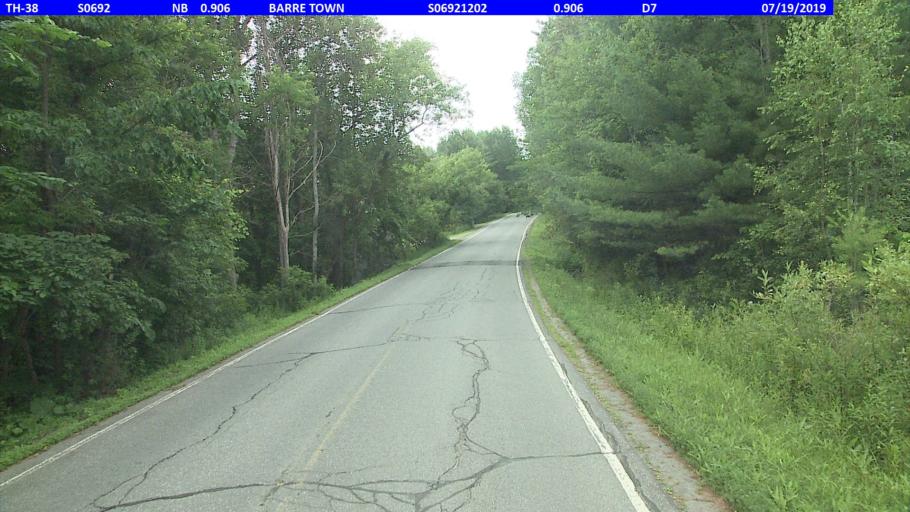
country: US
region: Vermont
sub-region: Washington County
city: South Barre
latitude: 44.1712
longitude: -72.4559
